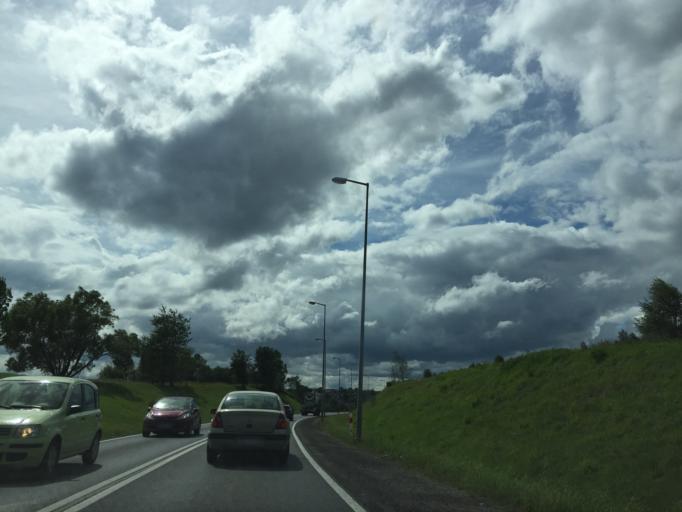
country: PL
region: Lesser Poland Voivodeship
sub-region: Powiat nowotarski
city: Nowy Targ
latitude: 49.4757
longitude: 20.0470
